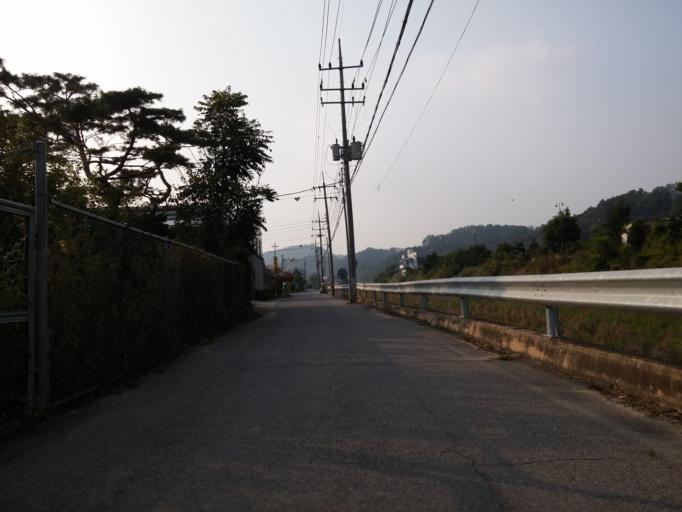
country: KR
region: Chungcheongbuk-do
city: Okcheon
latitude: 36.3312
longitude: 127.5313
